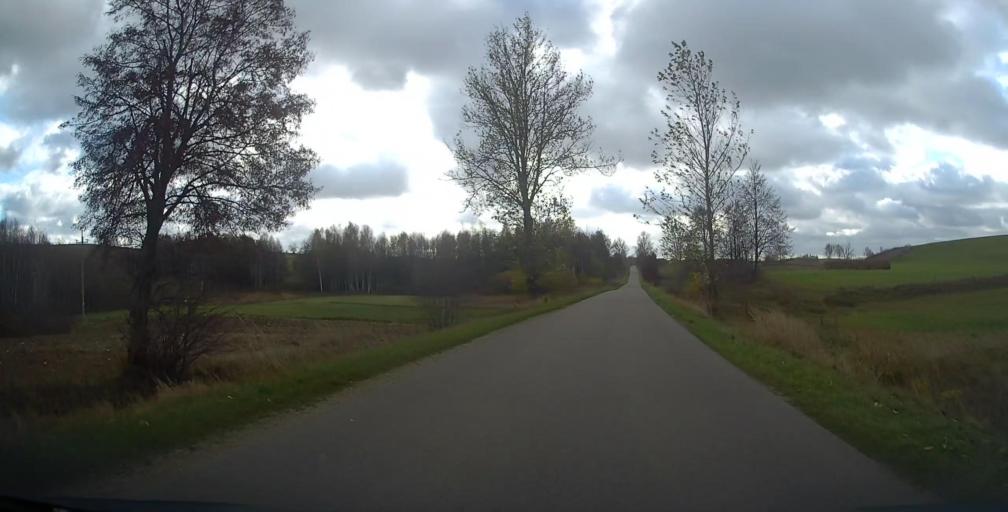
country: PL
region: Podlasie
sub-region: Suwalki
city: Suwalki
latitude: 54.3514
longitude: 22.8569
